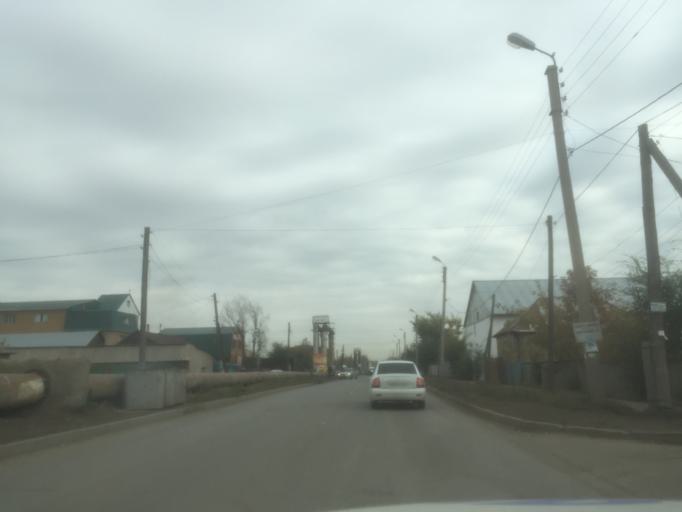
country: KZ
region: Astana Qalasy
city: Astana
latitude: 51.1866
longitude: 71.3901
